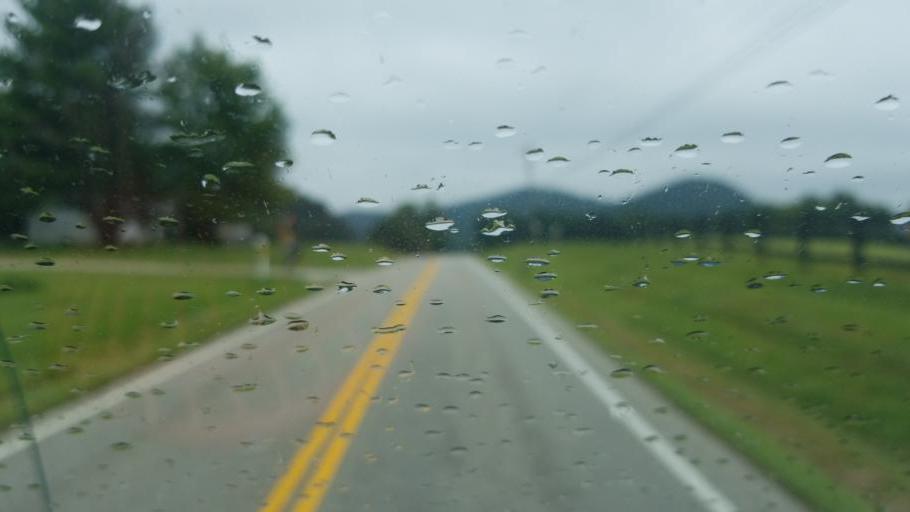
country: US
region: Kentucky
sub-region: Rowan County
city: Morehead
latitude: 38.2568
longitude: -83.4378
